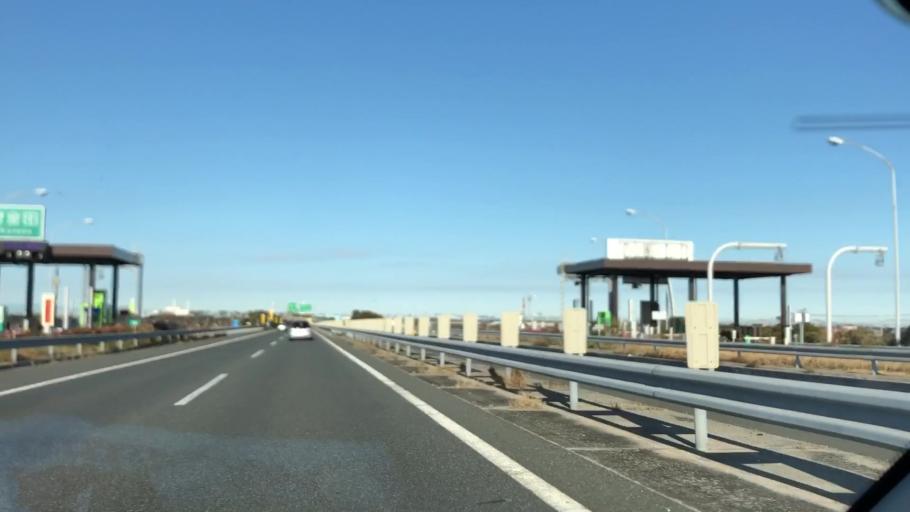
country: JP
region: Chiba
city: Kisarazu
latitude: 35.4279
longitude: 139.9286
